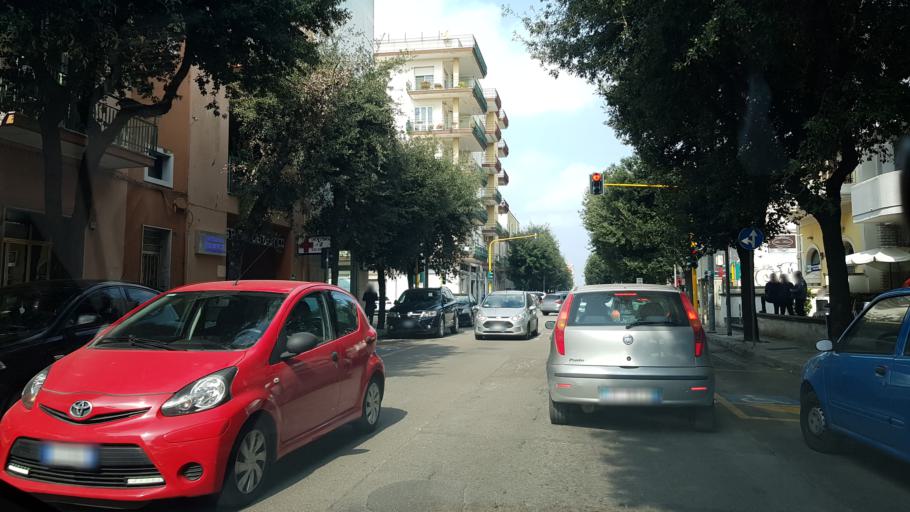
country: IT
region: Apulia
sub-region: Provincia di Lecce
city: Castromediano
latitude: 40.3389
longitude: 18.1771
